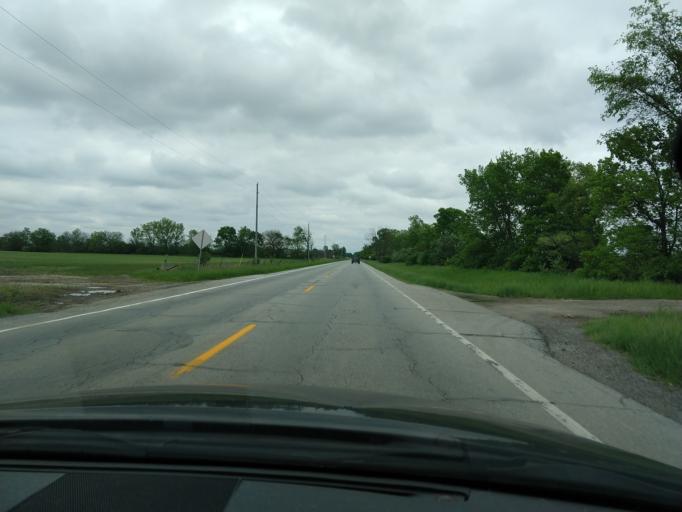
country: US
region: Indiana
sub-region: Hamilton County
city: Noblesville
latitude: 40.0450
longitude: -85.9649
